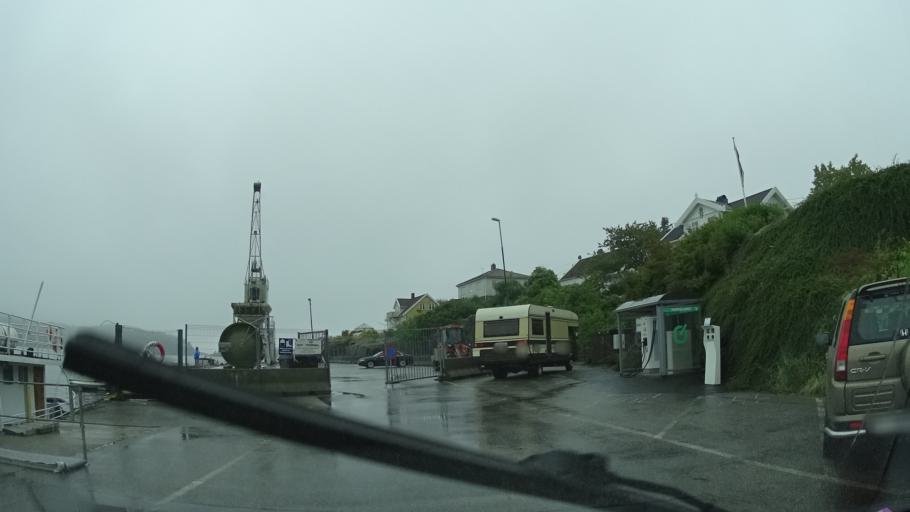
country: NO
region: Aust-Agder
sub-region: Lillesand
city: Lillesand
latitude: 58.2467
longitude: 8.3787
